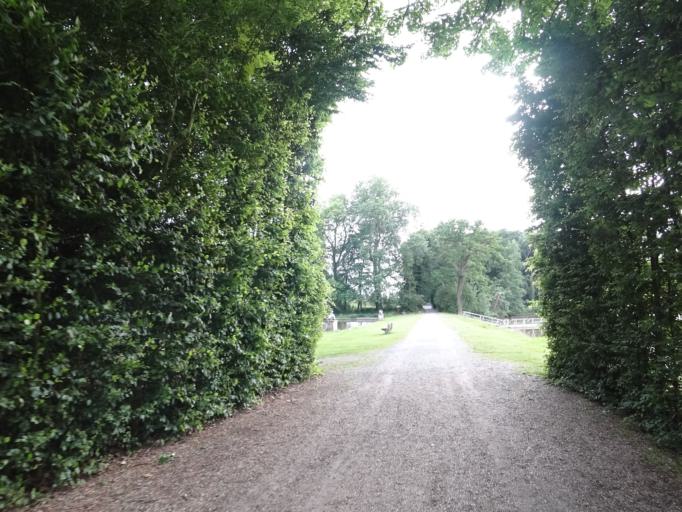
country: BE
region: Wallonia
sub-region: Province du Hainaut
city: Enghien
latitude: 50.6898
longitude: 4.0394
